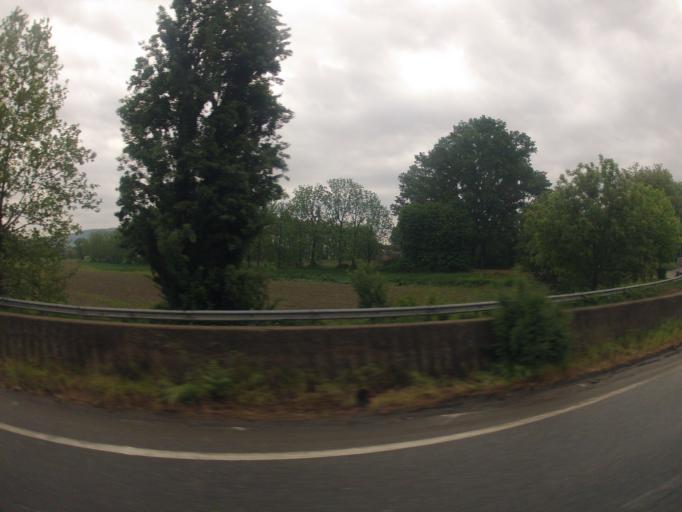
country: IT
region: Piedmont
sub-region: Provincia di Torino
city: Tagliaferro
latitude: 44.9679
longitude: 7.6700
